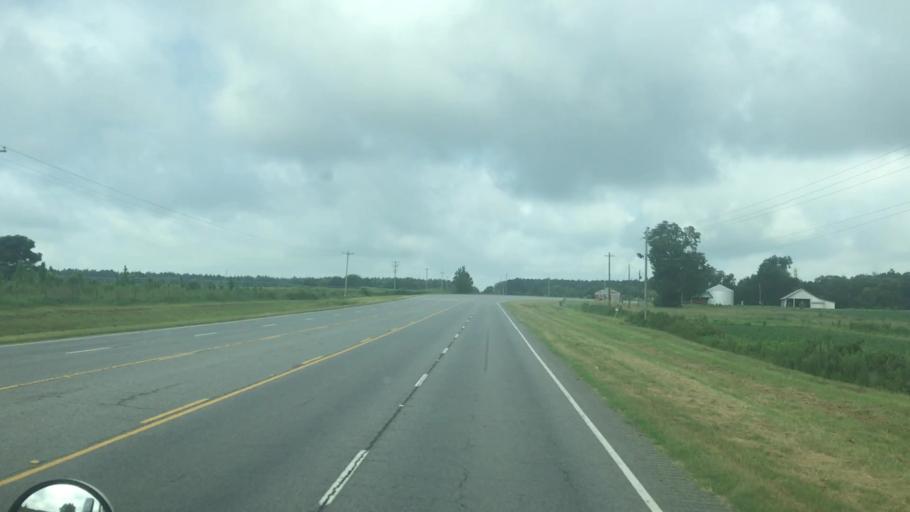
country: US
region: Georgia
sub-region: Miller County
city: Colquitt
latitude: 31.1697
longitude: -84.7491
